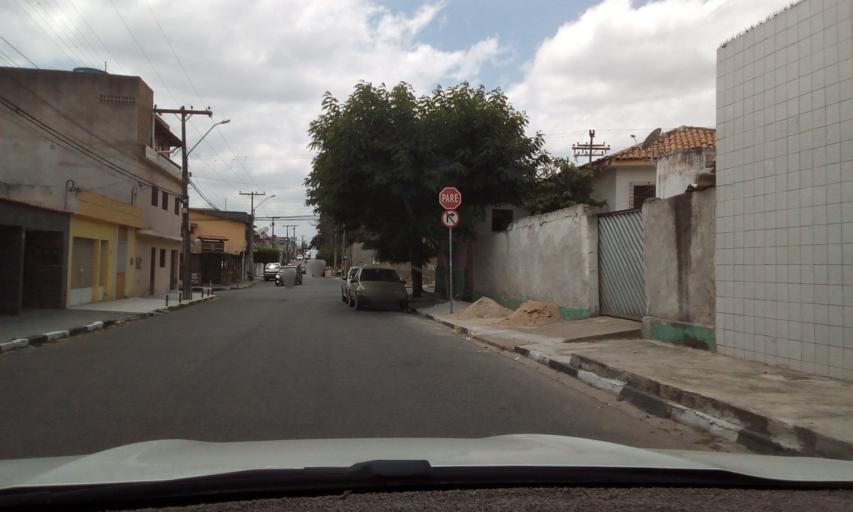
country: BR
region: Pernambuco
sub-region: Caruaru
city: Caruaru
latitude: -8.2759
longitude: -35.9776
